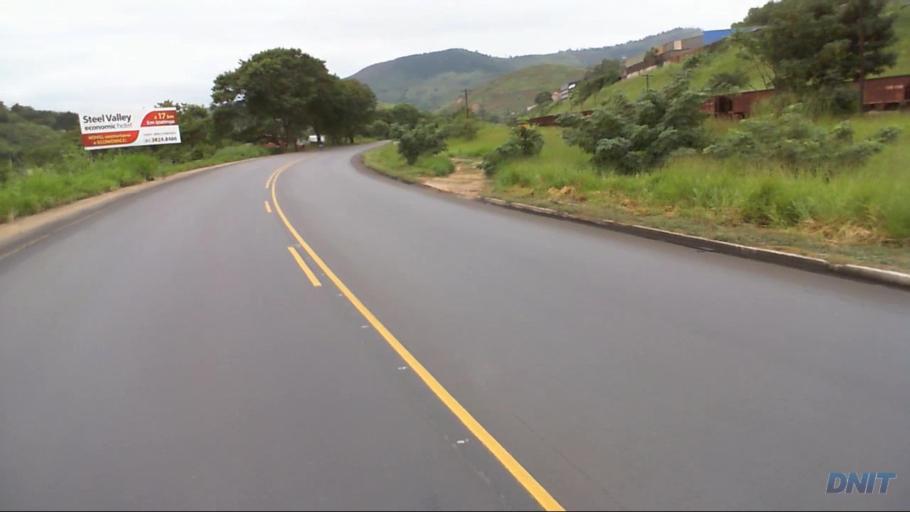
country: BR
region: Minas Gerais
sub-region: Coronel Fabriciano
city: Coronel Fabriciano
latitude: -19.5273
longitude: -42.6347
